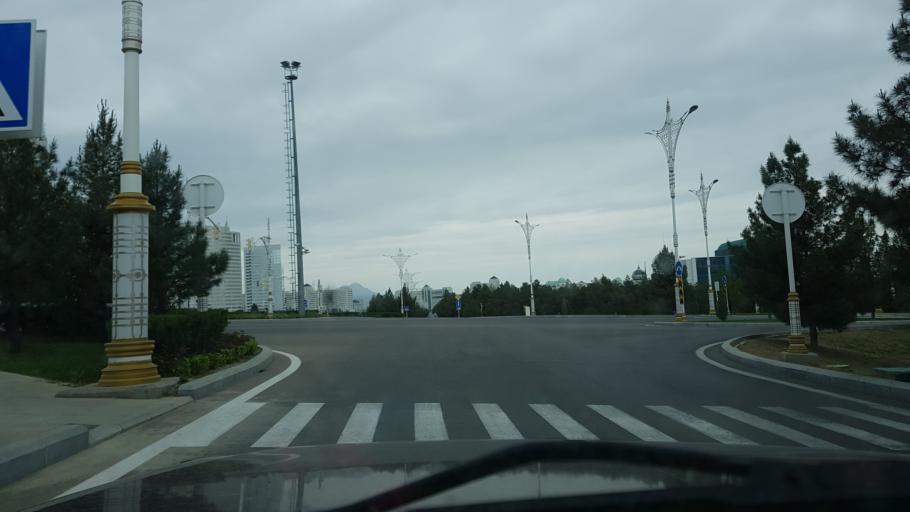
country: TM
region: Ahal
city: Ashgabat
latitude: 37.8881
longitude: 58.3527
